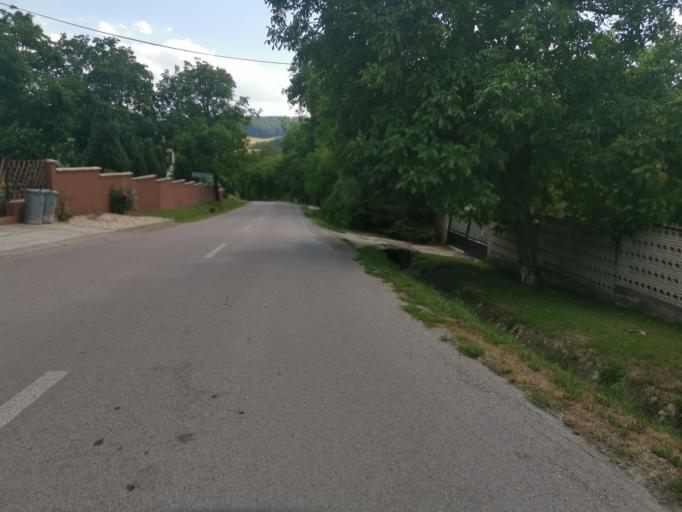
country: CZ
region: South Moravian
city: Knezdub
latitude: 48.8032
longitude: 17.4144
